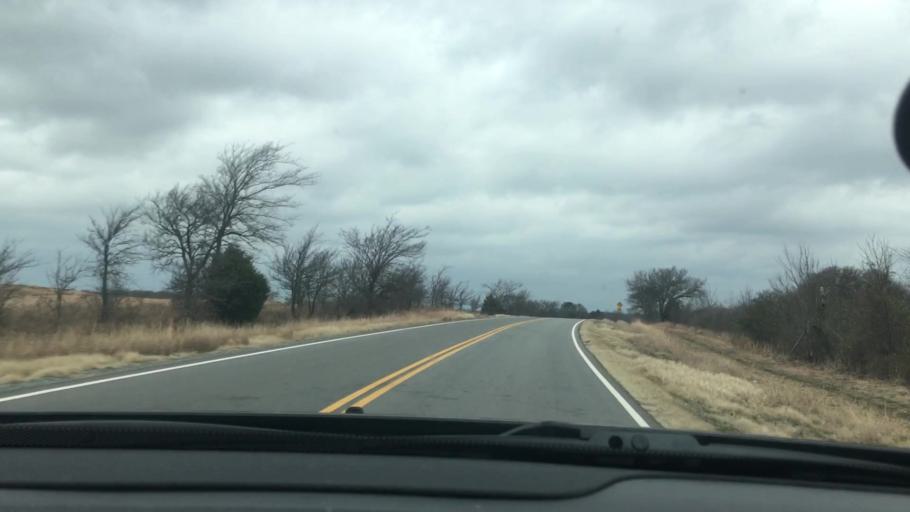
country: US
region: Oklahoma
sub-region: Atoka County
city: Atoka
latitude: 34.3758
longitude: -96.2606
